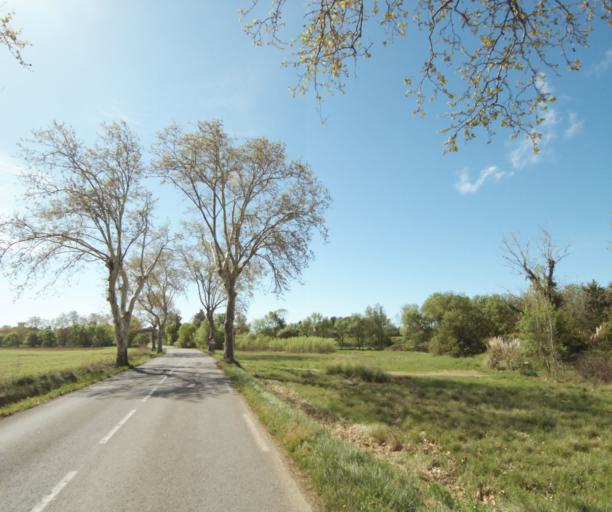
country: FR
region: Languedoc-Roussillon
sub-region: Departement de l'Herault
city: Villeneuve-les-Maguelone
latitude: 43.5474
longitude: 3.8470
